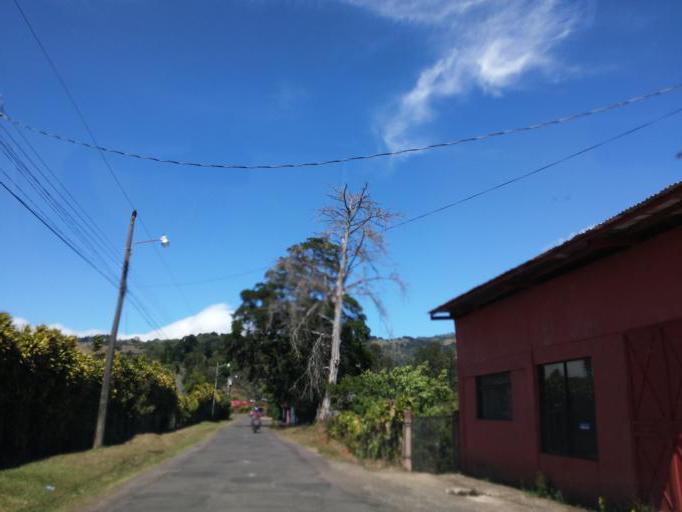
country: CR
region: Alajuela
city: Sabanilla
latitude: 10.1018
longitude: -84.1853
